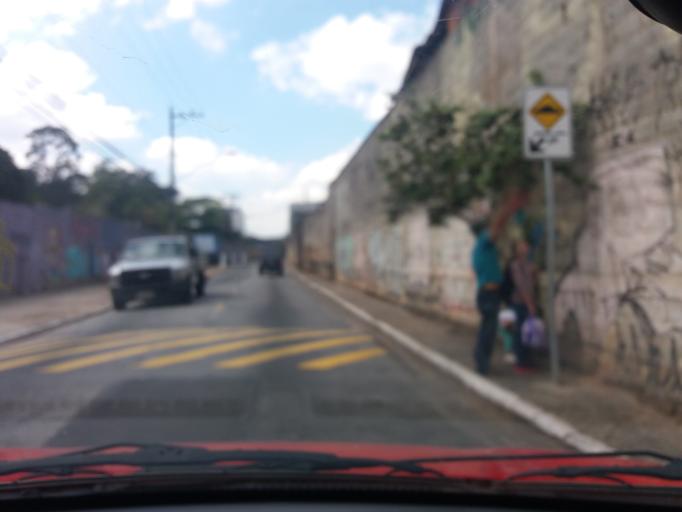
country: BR
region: Sao Paulo
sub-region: Taboao Da Serra
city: Taboao da Serra
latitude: -23.5961
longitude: -46.7476
